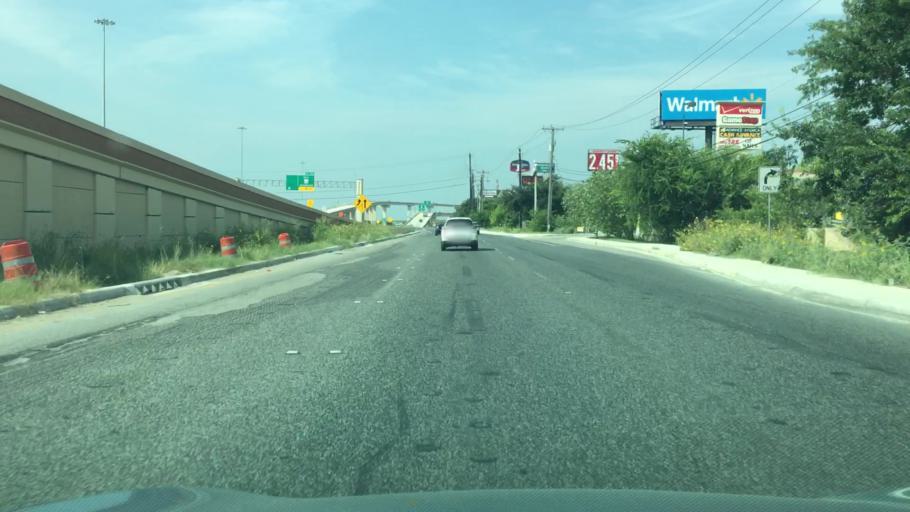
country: US
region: Texas
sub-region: Bexar County
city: Leon Valley
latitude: 29.4423
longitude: -98.6396
